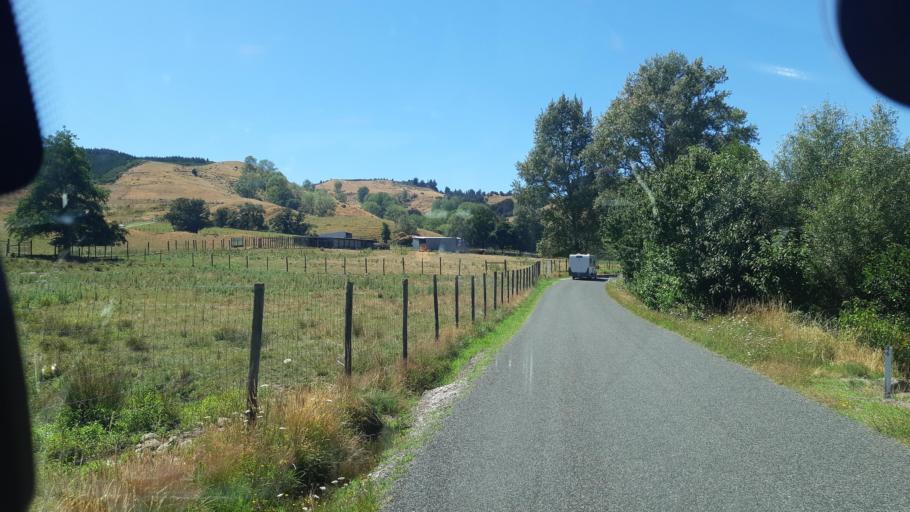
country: NZ
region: Tasman
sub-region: Tasman District
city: Motueka
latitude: -41.0413
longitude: 172.9133
